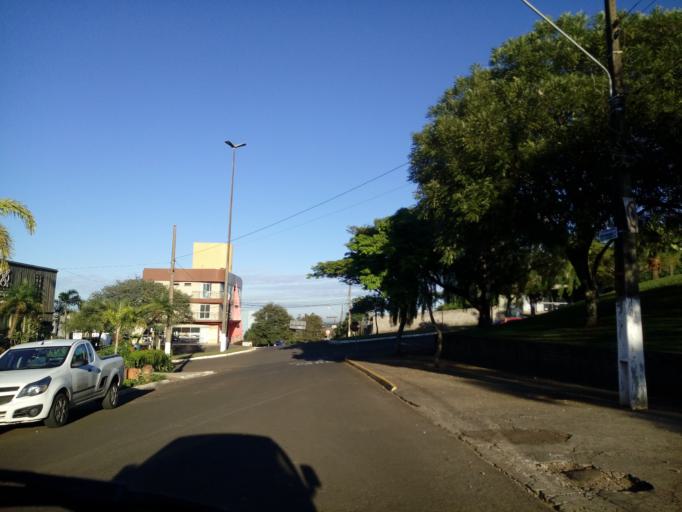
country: BR
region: Santa Catarina
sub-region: Chapeco
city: Chapeco
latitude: -27.1139
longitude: -52.6112
